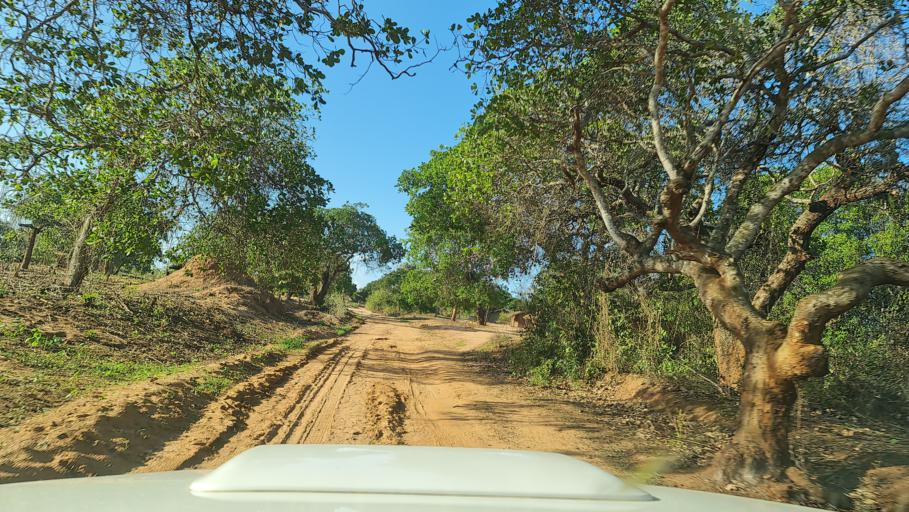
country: MZ
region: Nampula
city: Nacala
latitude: -14.6976
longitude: 40.3265
